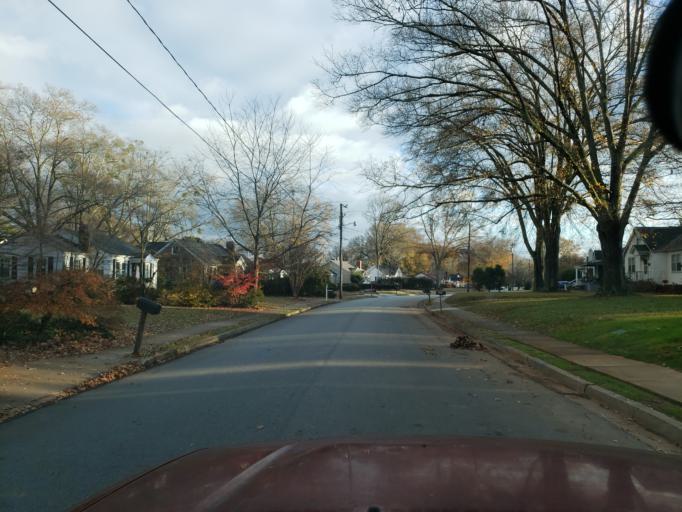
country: US
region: South Carolina
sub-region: Greenville County
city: Greenville
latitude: 34.8326
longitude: -82.3531
